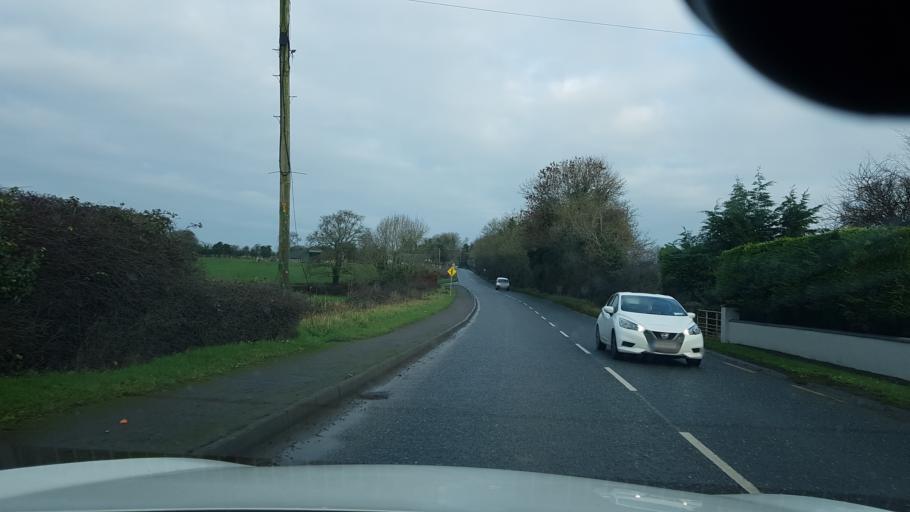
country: IE
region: Leinster
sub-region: An Mhi
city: Navan
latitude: 53.6736
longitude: -6.6773
